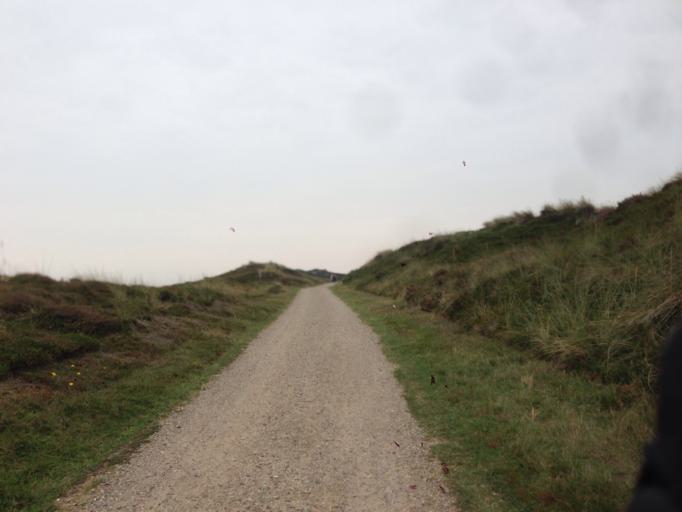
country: DE
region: Schleswig-Holstein
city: Westerland
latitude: 54.8233
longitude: 8.2933
